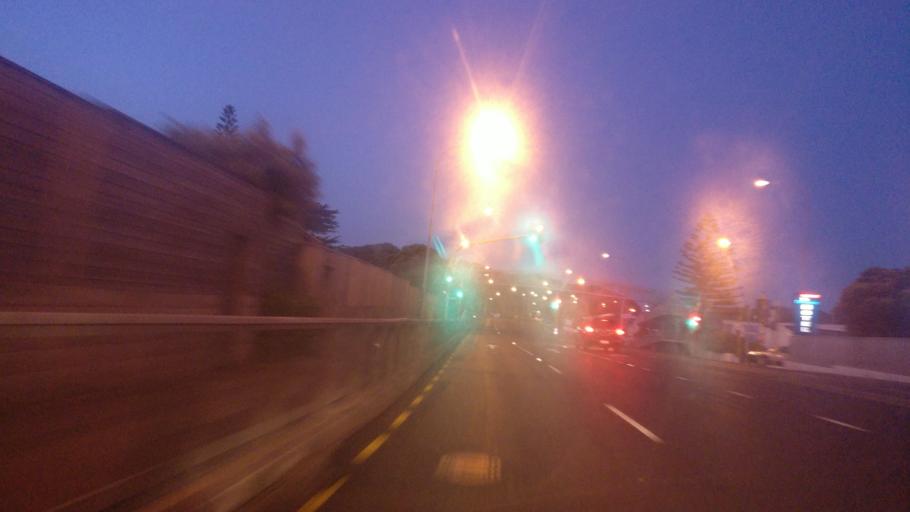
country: NZ
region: Wellington
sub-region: Porirua City
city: Porirua
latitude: -41.0861
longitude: 174.8686
